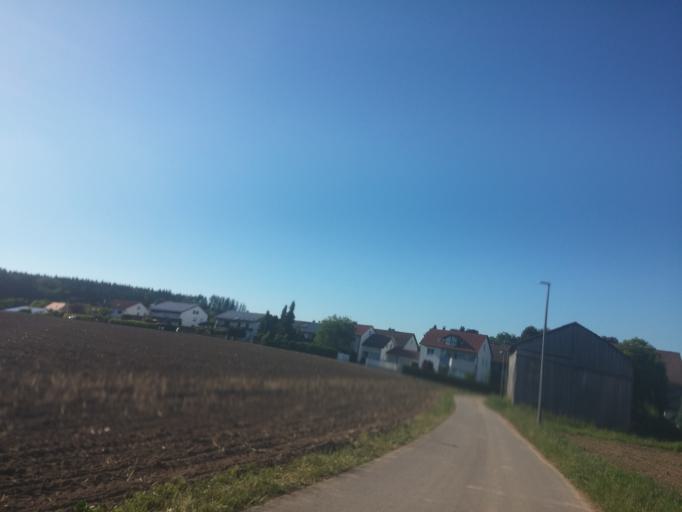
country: DE
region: Bavaria
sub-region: Swabia
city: Lautrach
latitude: 47.8932
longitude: 10.1163
